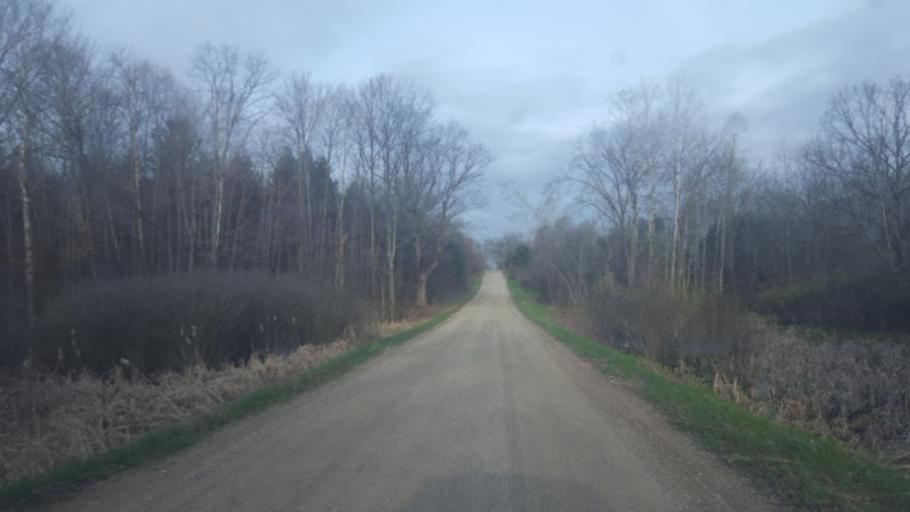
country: US
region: Michigan
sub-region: Isabella County
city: Lake Isabella
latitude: 43.5674
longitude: -84.9893
